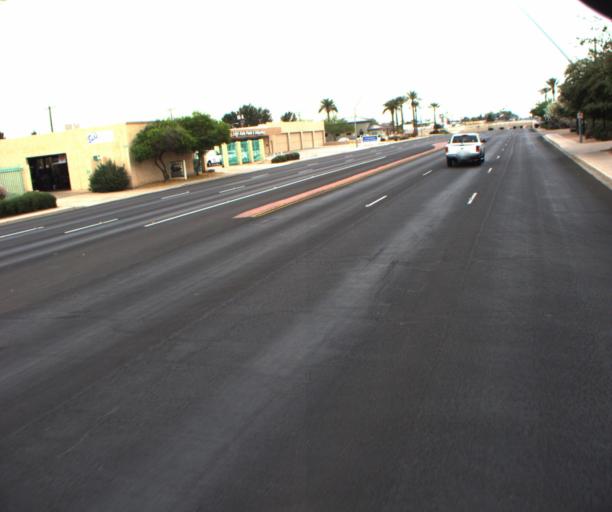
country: US
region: Arizona
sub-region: Maricopa County
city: Mesa
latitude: 33.4125
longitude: -111.8400
